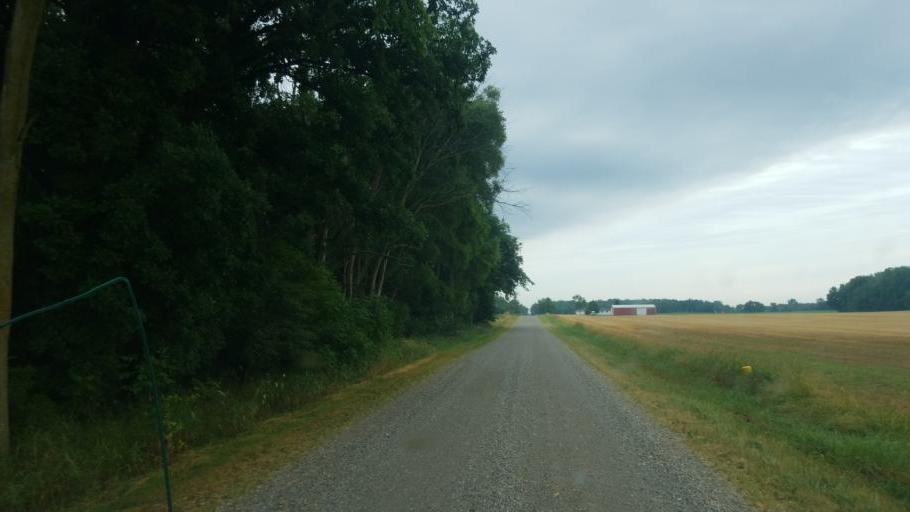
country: US
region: Indiana
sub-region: Steuben County
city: Hamilton
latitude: 41.4907
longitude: -84.9109
